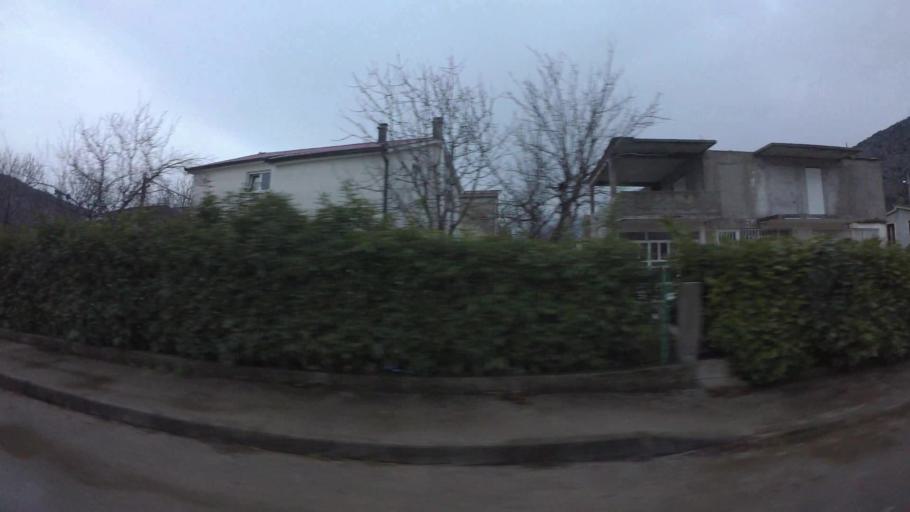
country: BA
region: Federation of Bosnia and Herzegovina
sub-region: Hercegovacko-Bosanski Kanton
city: Mostar
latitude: 43.3679
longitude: 17.8215
